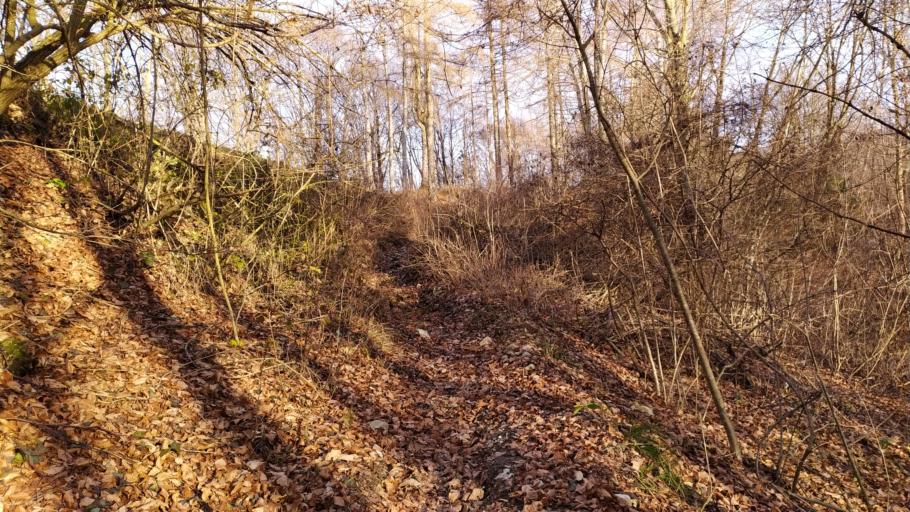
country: IT
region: Veneto
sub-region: Provincia di Vicenza
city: Velo d'Astico
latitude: 45.7680
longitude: 11.3624
